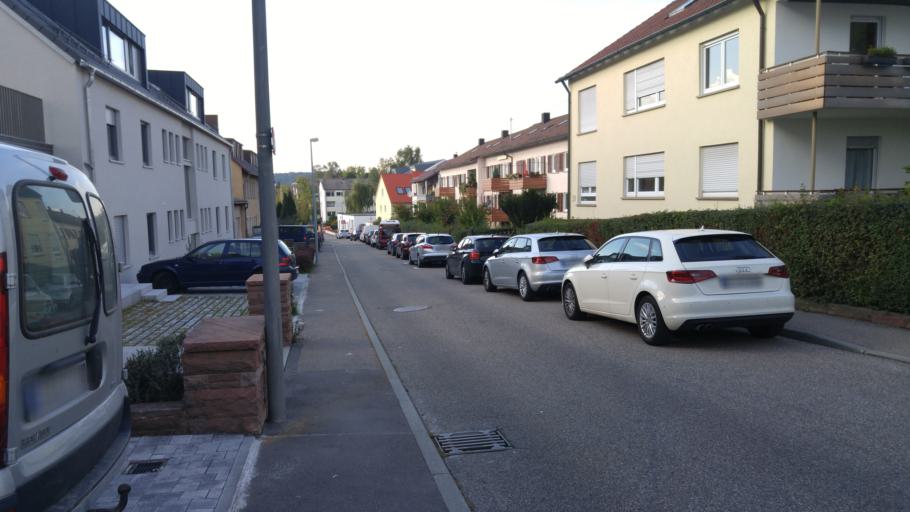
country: DE
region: Baden-Wuerttemberg
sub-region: Regierungsbezirk Stuttgart
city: Leonberg
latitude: 48.8053
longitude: 9.0134
